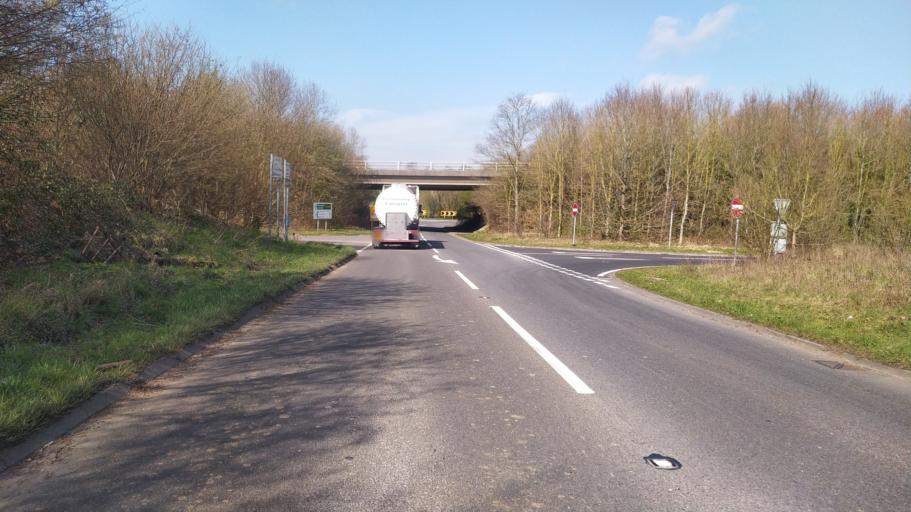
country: GB
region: England
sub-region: Somerset
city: Stoke-sub-Hamdon
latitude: 50.9495
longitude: -2.7725
